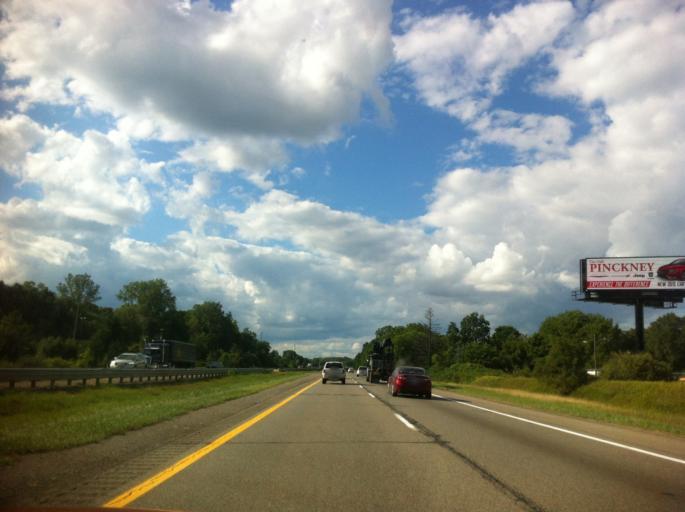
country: US
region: Michigan
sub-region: Livingston County
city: Whitmore Lake
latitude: 42.4128
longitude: -83.7643
